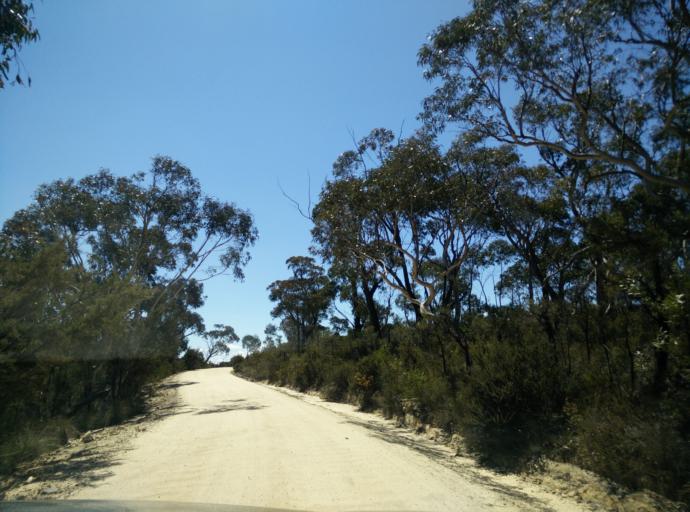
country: AU
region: New South Wales
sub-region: Blue Mountains Municipality
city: Blackheath
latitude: -33.5731
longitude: 150.2775
